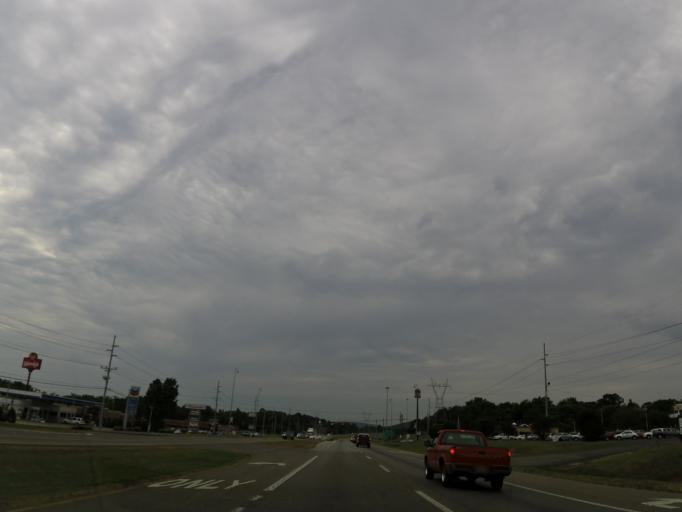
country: US
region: Alabama
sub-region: Jackson County
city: Scottsboro
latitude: 34.6492
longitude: -86.0308
